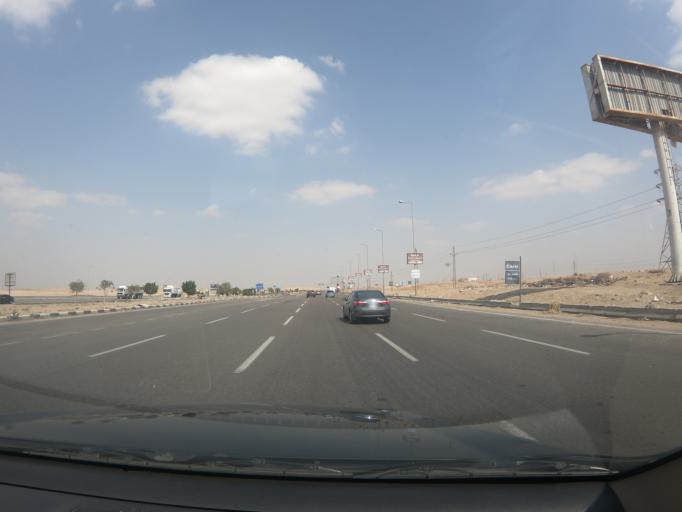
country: EG
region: Muhafazat al Qalyubiyah
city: Al Khankah
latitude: 30.0856
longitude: 31.4854
